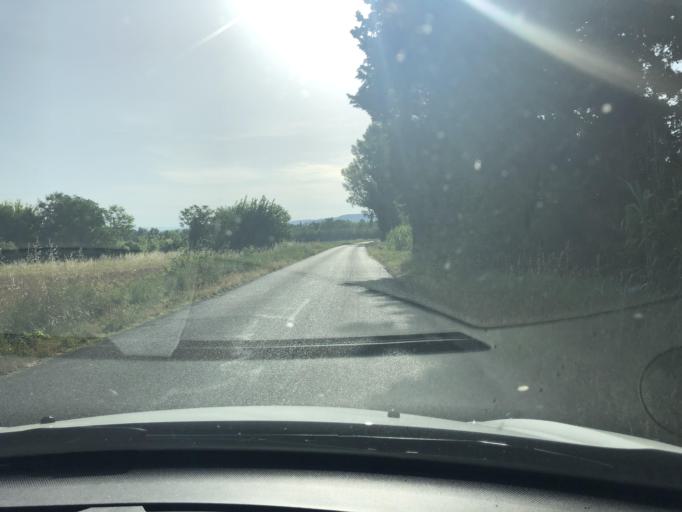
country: FR
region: Provence-Alpes-Cote d'Azur
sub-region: Departement du Vaucluse
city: Velleron
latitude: 43.9657
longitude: 5.0054
